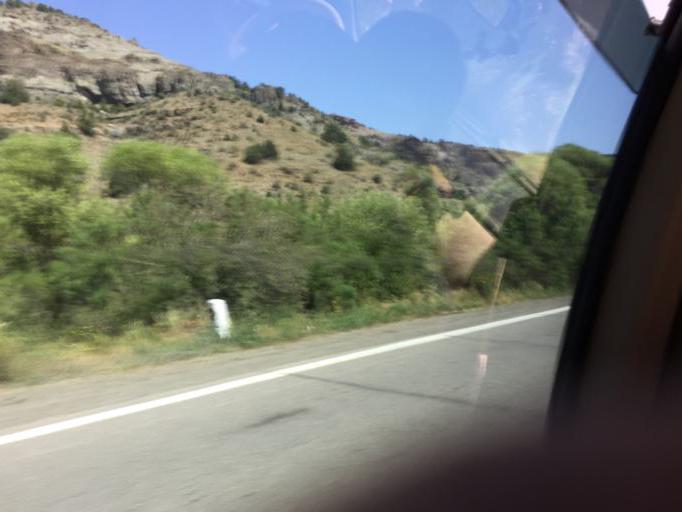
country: AM
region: Vayots' Dzori Marz
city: Zarrit'ap'
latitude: 39.6960
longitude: 45.5750
